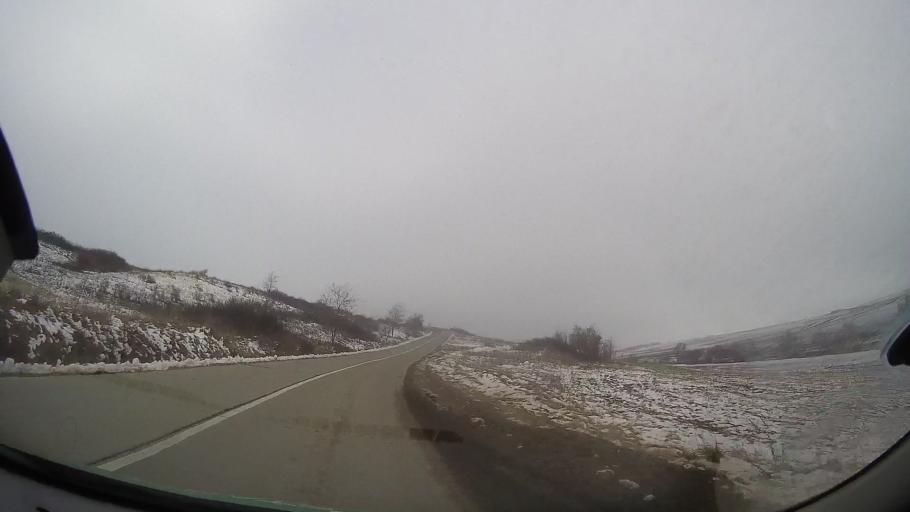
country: RO
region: Vaslui
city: Coroiesti
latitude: 46.2167
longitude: 27.4713
